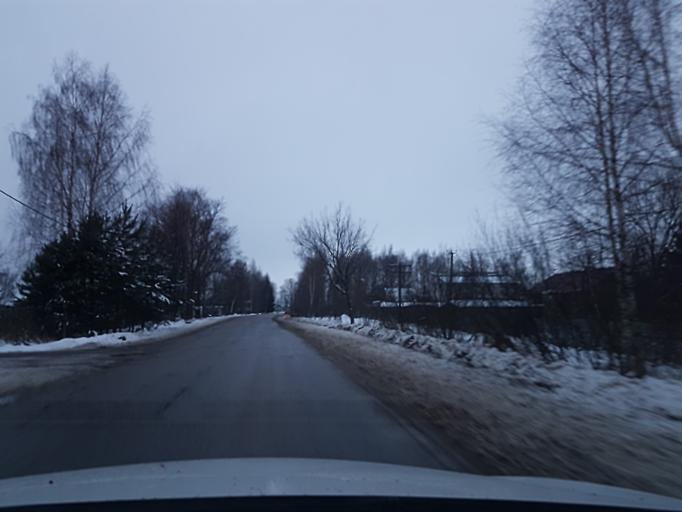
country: RU
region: Tverskaya
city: Novozavidovskiy
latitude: 56.5581
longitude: 36.4172
